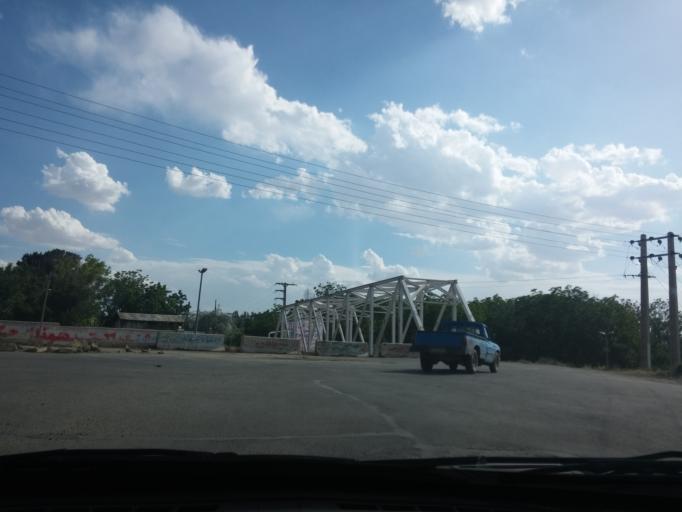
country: IR
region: Tehran
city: Damavand
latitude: 35.7254
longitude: 51.9017
